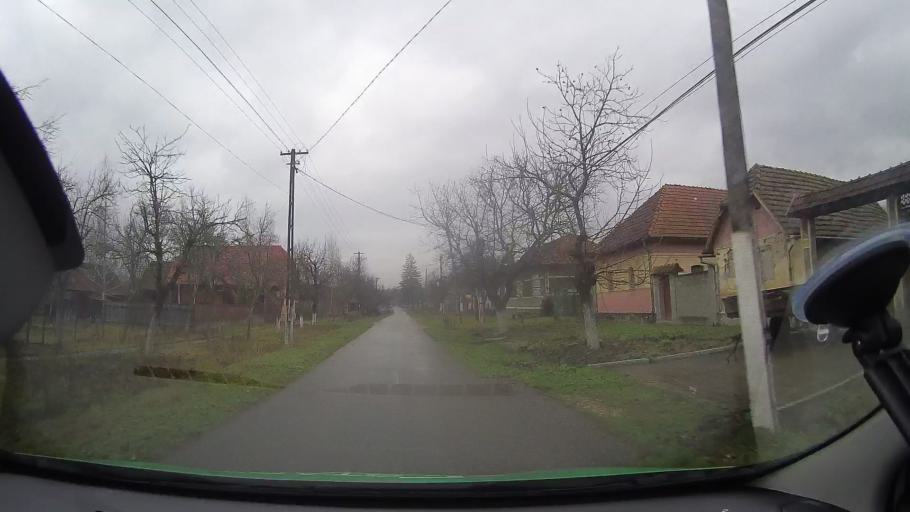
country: RO
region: Arad
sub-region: Comuna Brazii
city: Brazii
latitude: 46.2392
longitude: 22.3333
